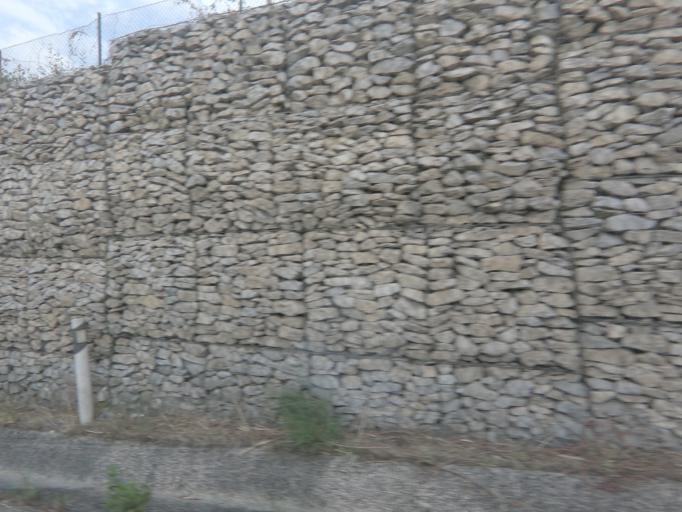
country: PT
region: Coimbra
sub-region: Coimbra
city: Coimbra
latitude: 40.2126
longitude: -8.4463
